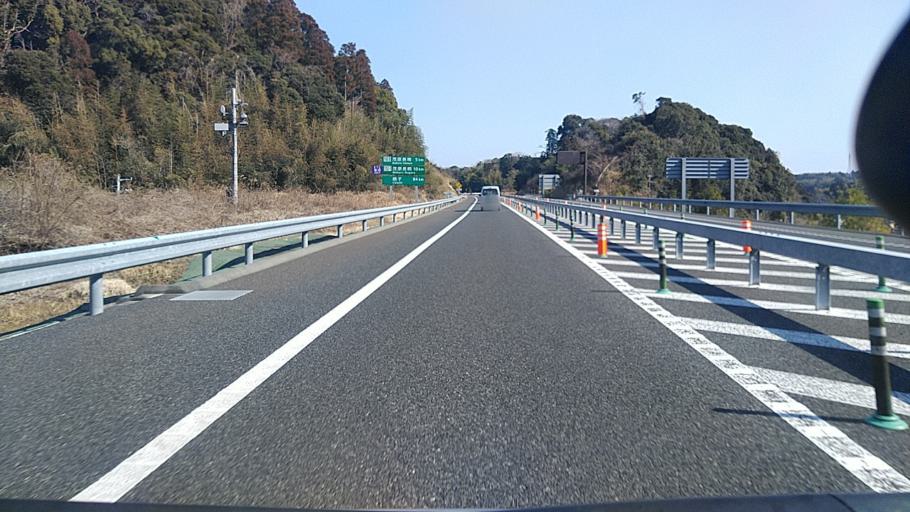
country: JP
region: Chiba
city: Mobara
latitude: 35.3710
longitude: 140.2141
